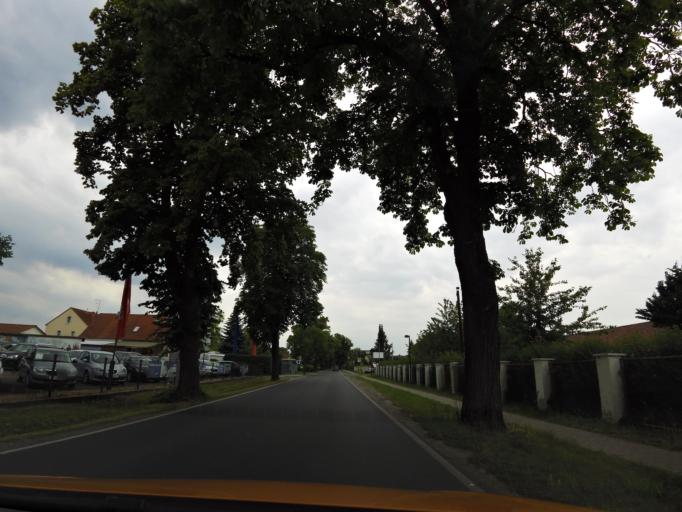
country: DE
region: Brandenburg
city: Zossen
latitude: 52.2223
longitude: 13.4302
